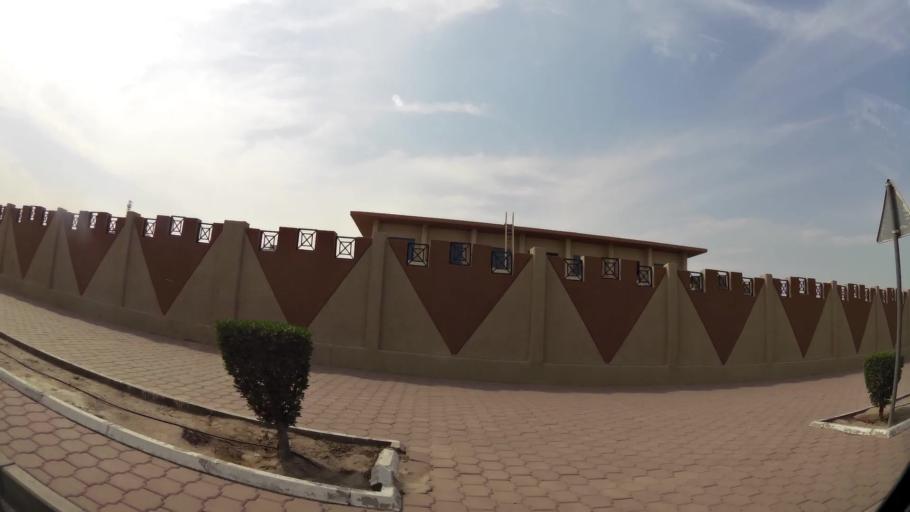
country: KW
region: Al Asimah
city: Ash Shamiyah
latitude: 29.3406
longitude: 47.9804
